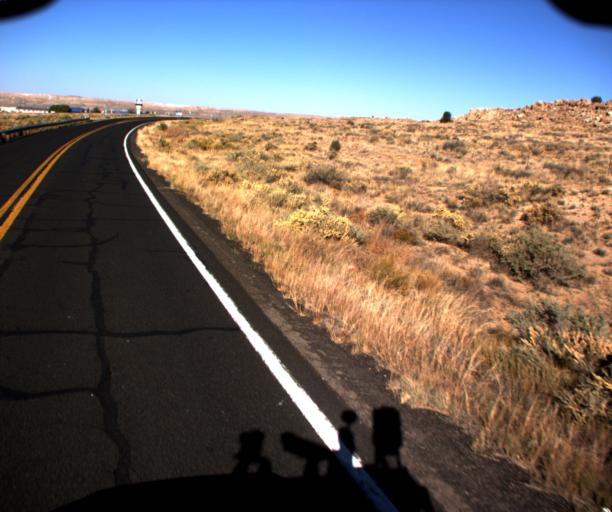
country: US
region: Arizona
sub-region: Navajo County
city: First Mesa
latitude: 35.8307
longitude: -110.2905
